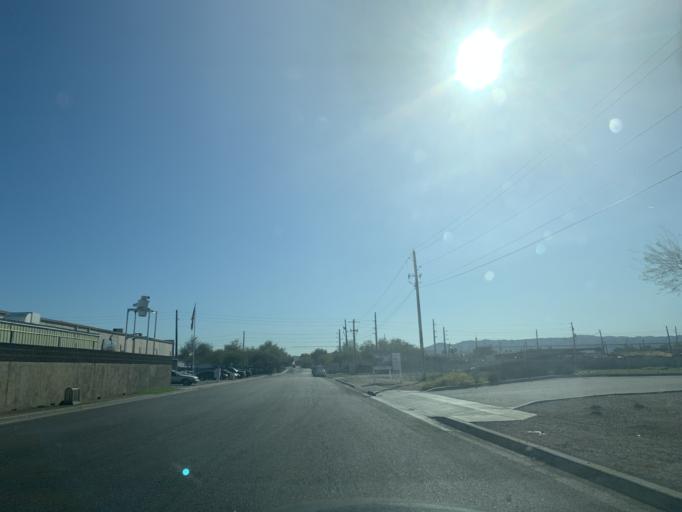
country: US
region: Arizona
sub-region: Maricopa County
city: Tempe Junction
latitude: 33.4195
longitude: -111.9870
